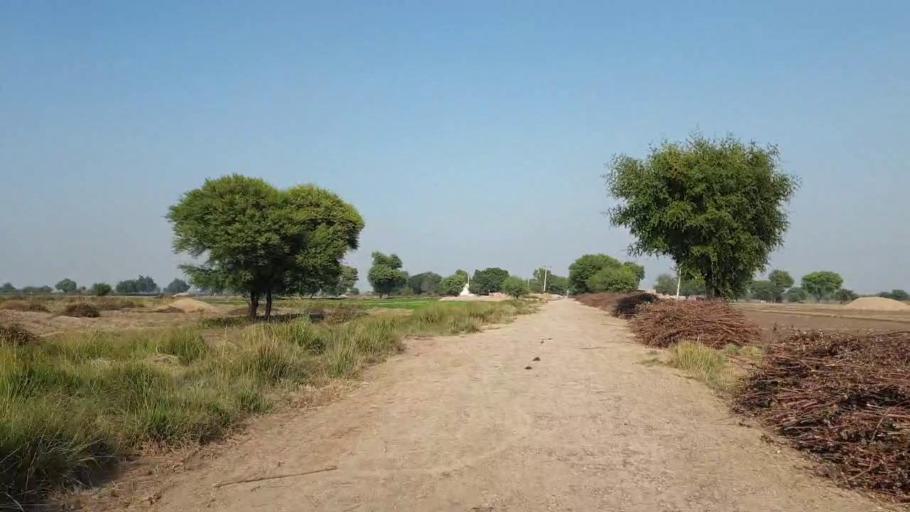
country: PK
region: Sindh
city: Sehwan
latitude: 26.4597
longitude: 67.8152
